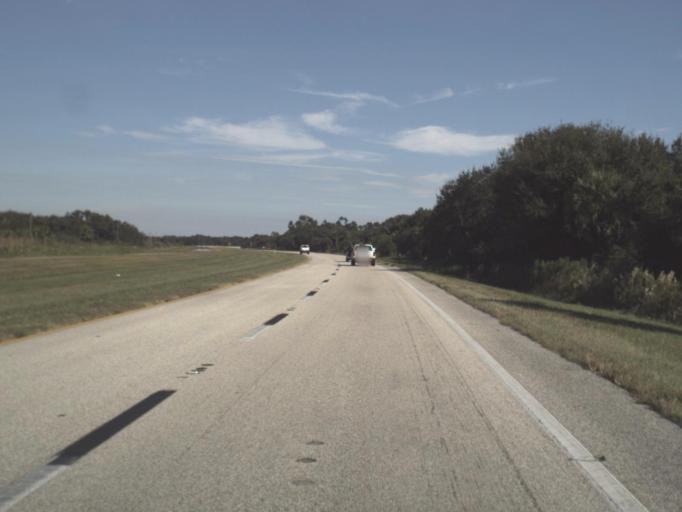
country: US
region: Florida
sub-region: Glades County
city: Moore Haven
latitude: 26.9021
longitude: -81.2523
